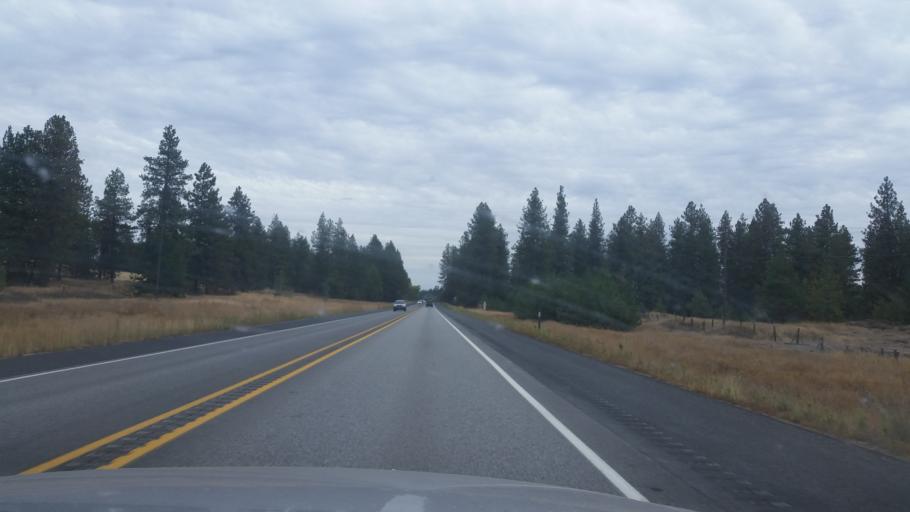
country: US
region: Washington
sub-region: Spokane County
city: Cheney
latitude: 47.5377
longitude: -117.5773
